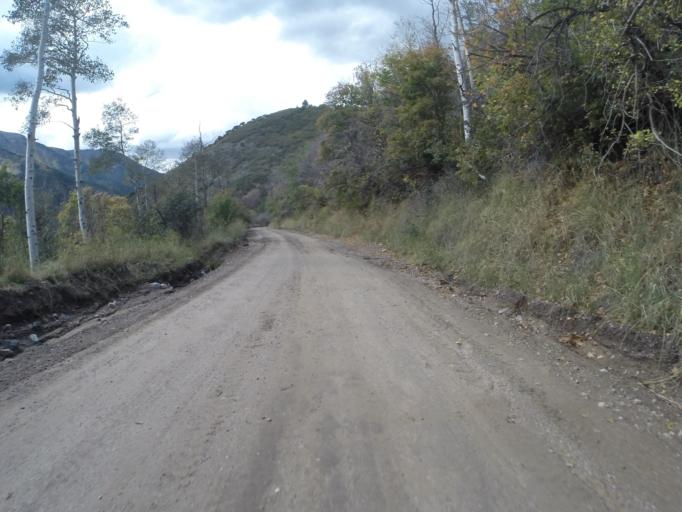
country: US
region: Utah
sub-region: Tooele County
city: Tooele
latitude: 40.4852
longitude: -112.1792
